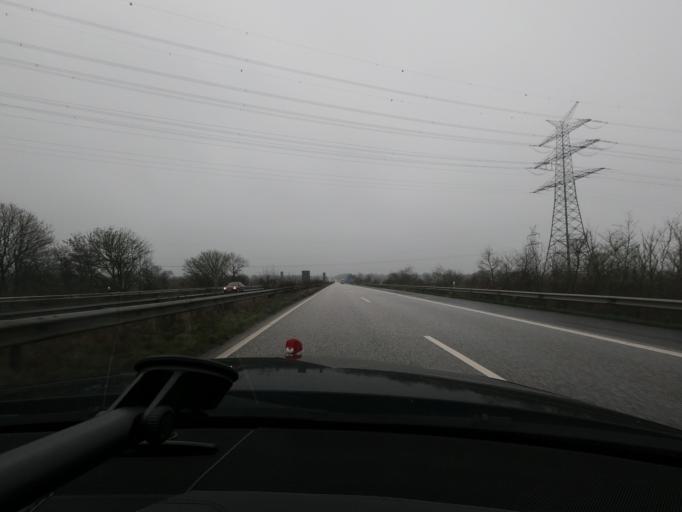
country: DE
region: Schleswig-Holstein
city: Schulldorf
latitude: 54.2970
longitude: 9.7605
